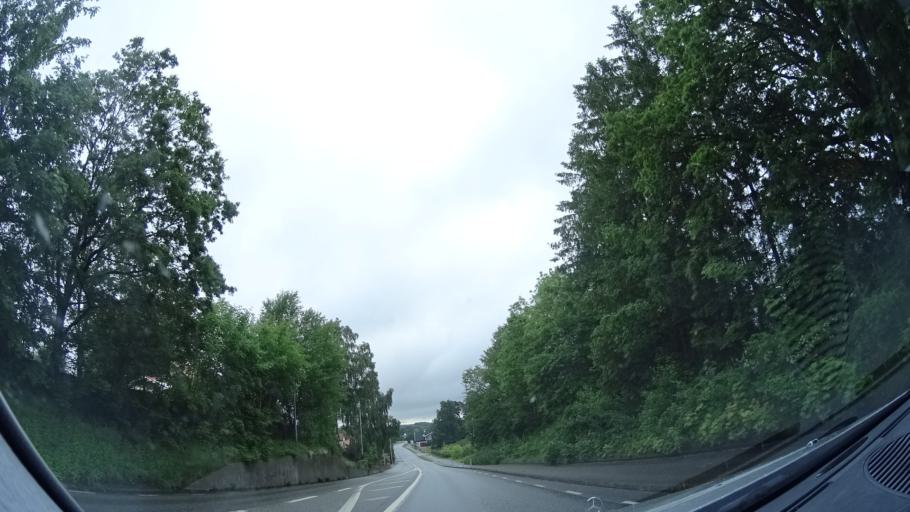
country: SE
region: Skane
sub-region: Hoors Kommun
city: Satofta
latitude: 55.9223
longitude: 13.5416
